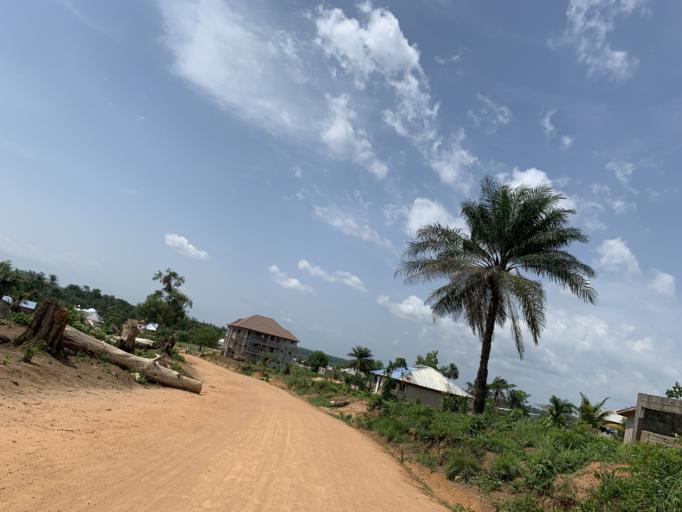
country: SL
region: Western Area
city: Waterloo
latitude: 8.3631
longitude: -13.0429
